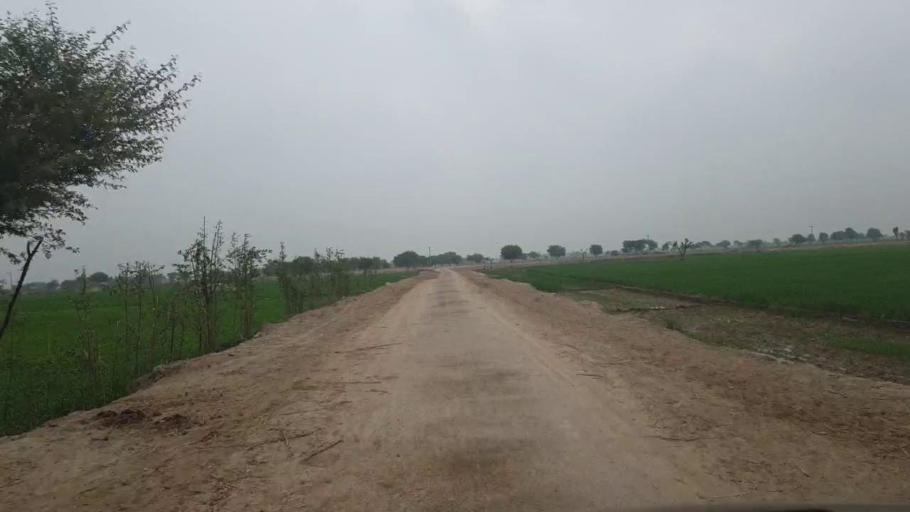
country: PK
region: Sindh
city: Tando Adam
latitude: 25.8611
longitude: 68.7078
